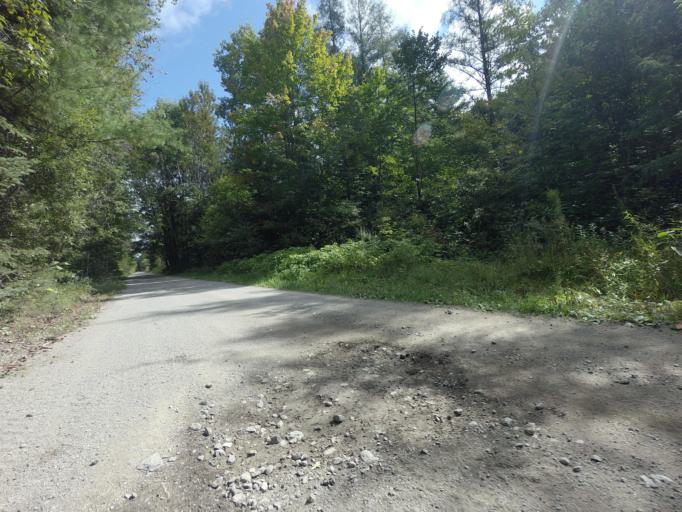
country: CA
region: Ontario
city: Omemee
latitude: 44.7337
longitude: -78.6755
